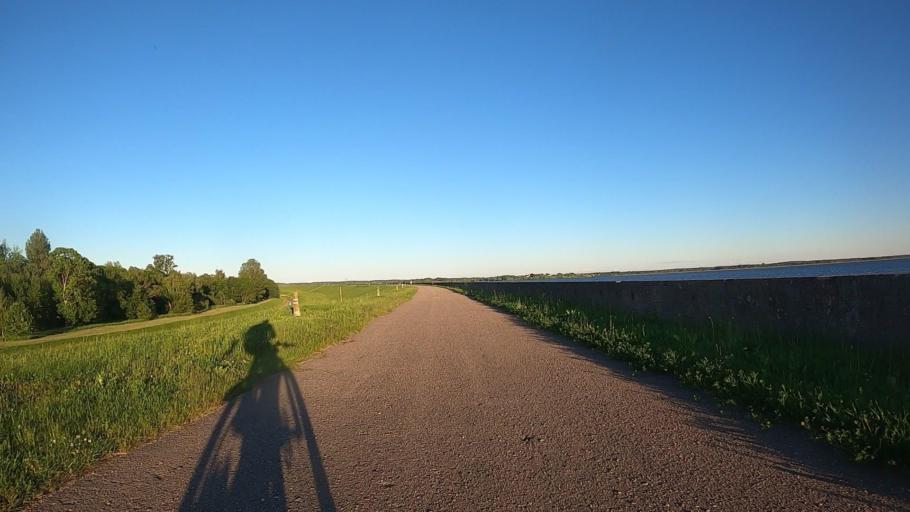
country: LV
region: Salaspils
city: Salaspils
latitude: 56.8530
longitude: 24.3212
